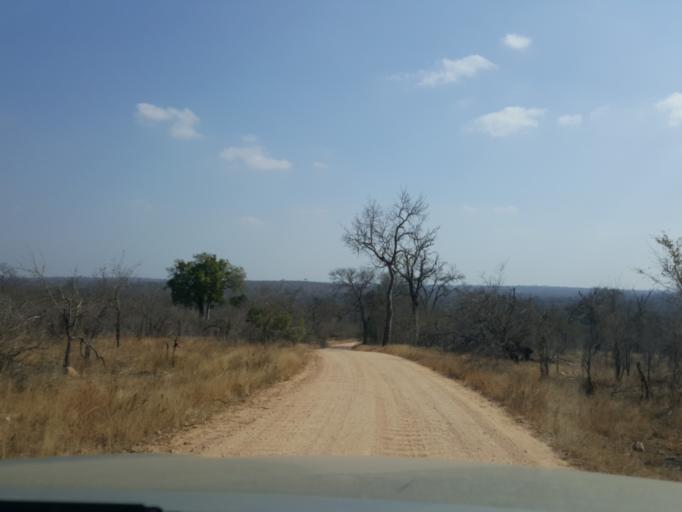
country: ZA
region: Mpumalanga
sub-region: Ehlanzeni District
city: Komatipoort
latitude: -25.2729
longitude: 31.7857
